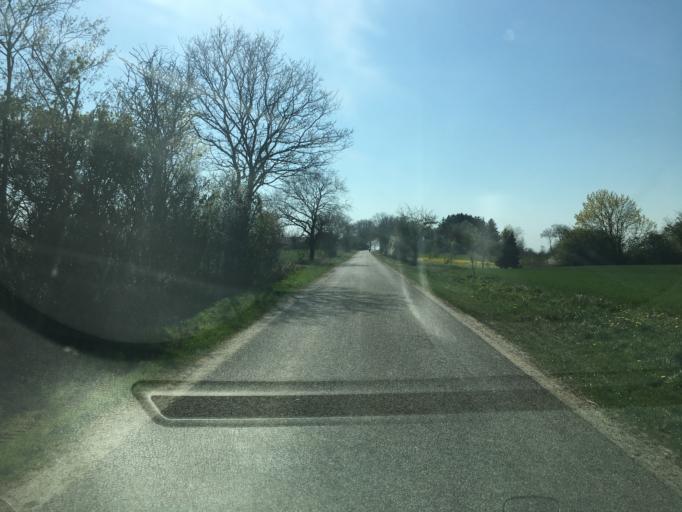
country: DK
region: South Denmark
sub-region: Aabenraa Kommune
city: Rodekro
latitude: 55.0005
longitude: 9.3323
